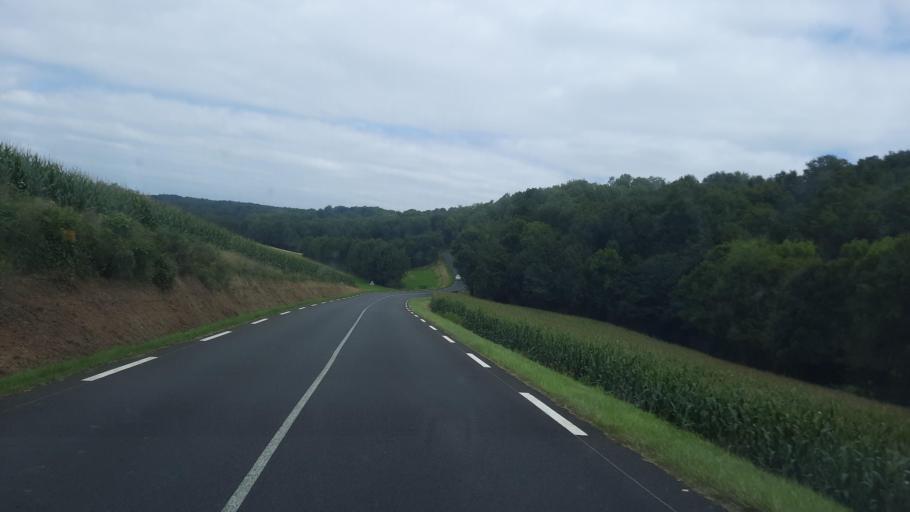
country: FR
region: Midi-Pyrenees
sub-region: Departement des Hautes-Pyrenees
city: Orleix
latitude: 43.2596
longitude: 0.1500
